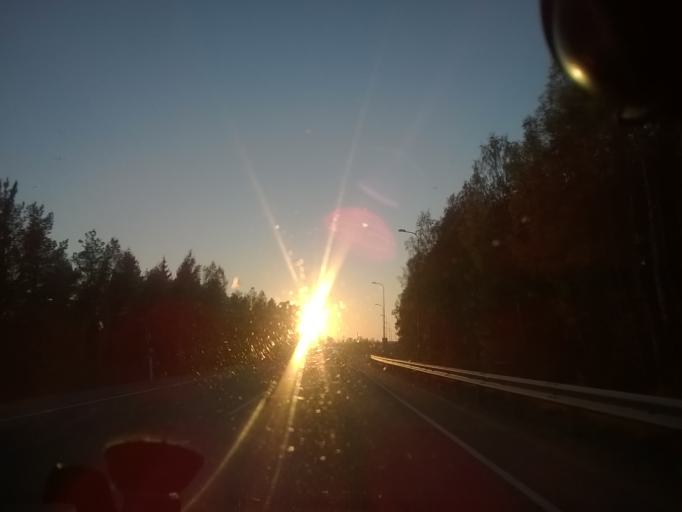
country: EE
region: Harju
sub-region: Nissi vald
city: Turba
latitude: 58.9941
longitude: 24.0629
